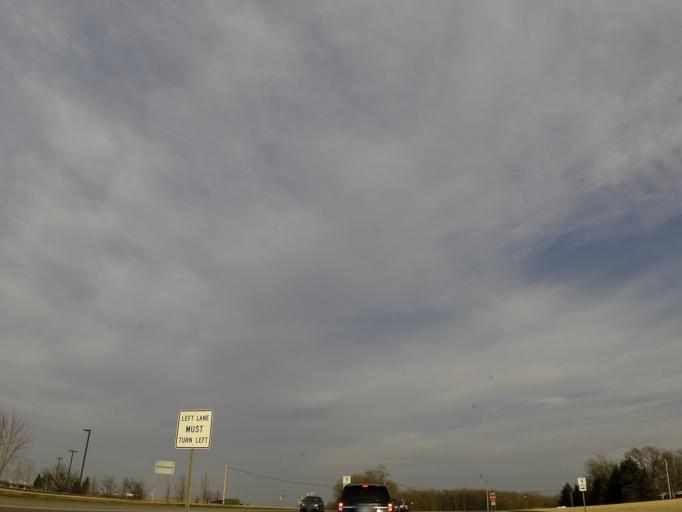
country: US
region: Minnesota
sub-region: Dakota County
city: Lakeville
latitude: 44.6813
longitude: -93.2529
